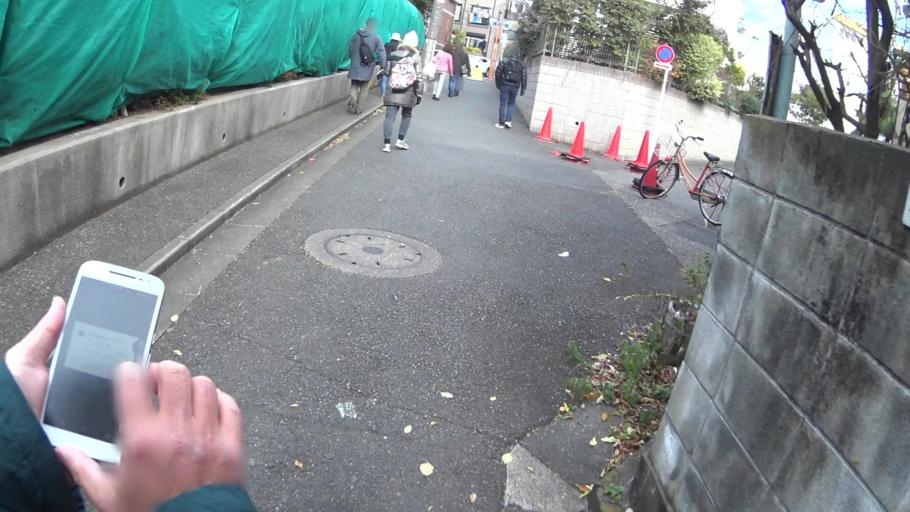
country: JP
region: Tokyo
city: Tokyo
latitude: 35.6760
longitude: 139.6835
